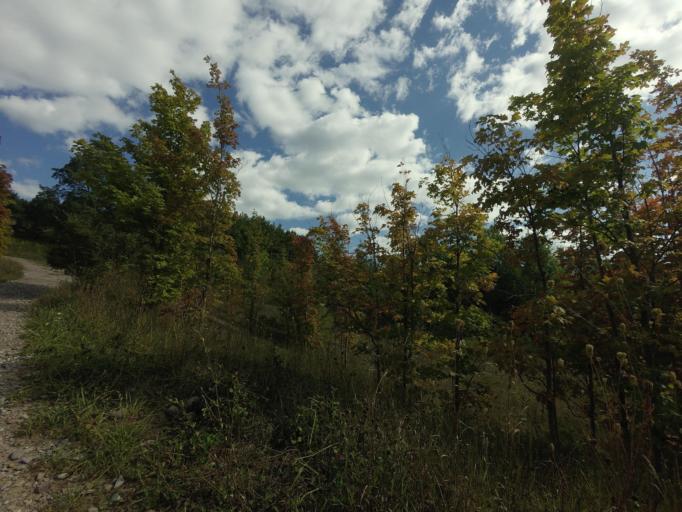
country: CA
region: Ontario
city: Orangeville
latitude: 43.8243
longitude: -80.0047
